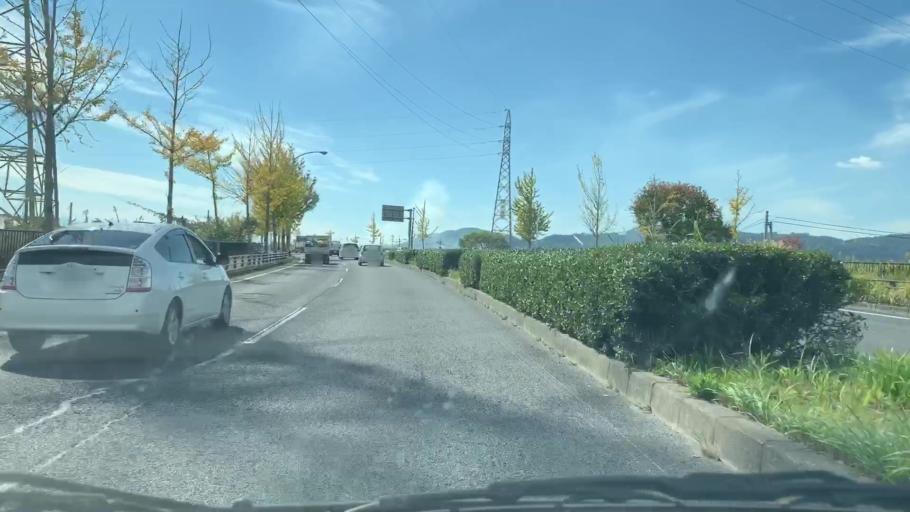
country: JP
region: Saga Prefecture
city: Saga-shi
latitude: 33.2566
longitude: 130.2007
